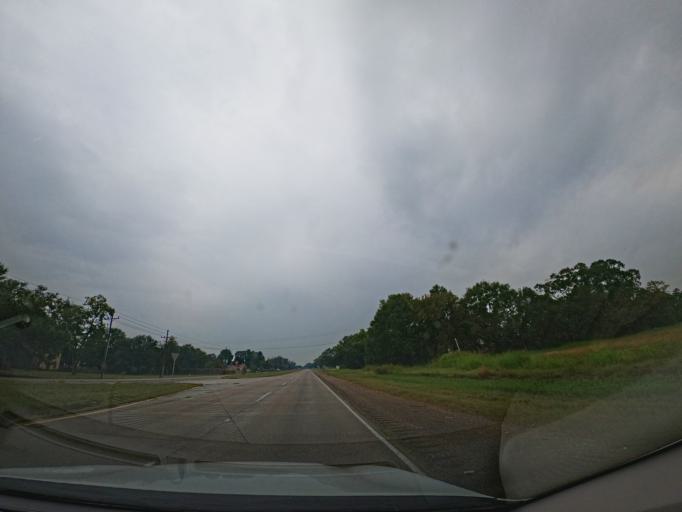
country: US
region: Louisiana
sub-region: Iberia Parish
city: New Iberia
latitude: 29.9854
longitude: -91.8782
